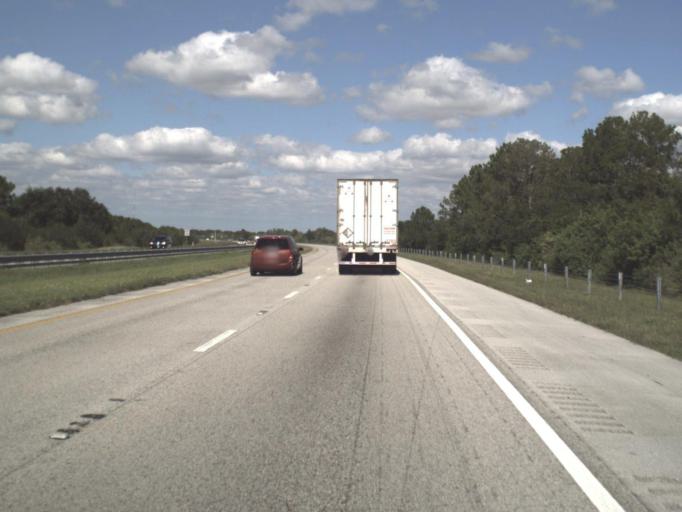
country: US
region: Florida
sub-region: Osceola County
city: Buenaventura Lakes
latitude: 28.2806
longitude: -81.3377
